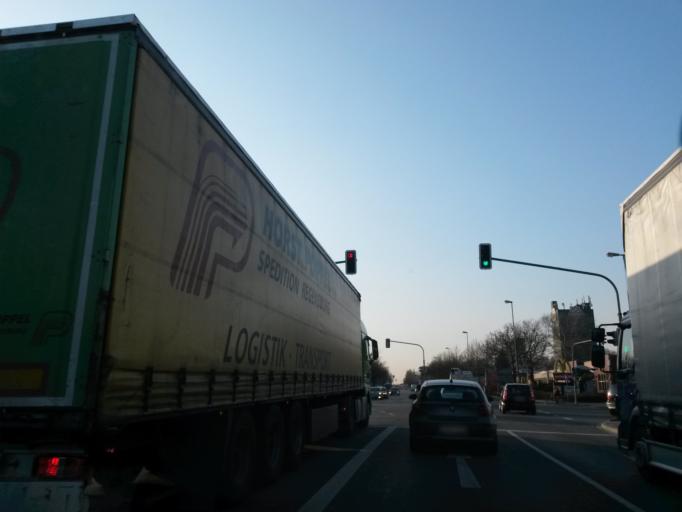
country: DE
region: Bavaria
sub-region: Upper Bavaria
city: Manching
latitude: 48.7464
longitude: 11.4675
